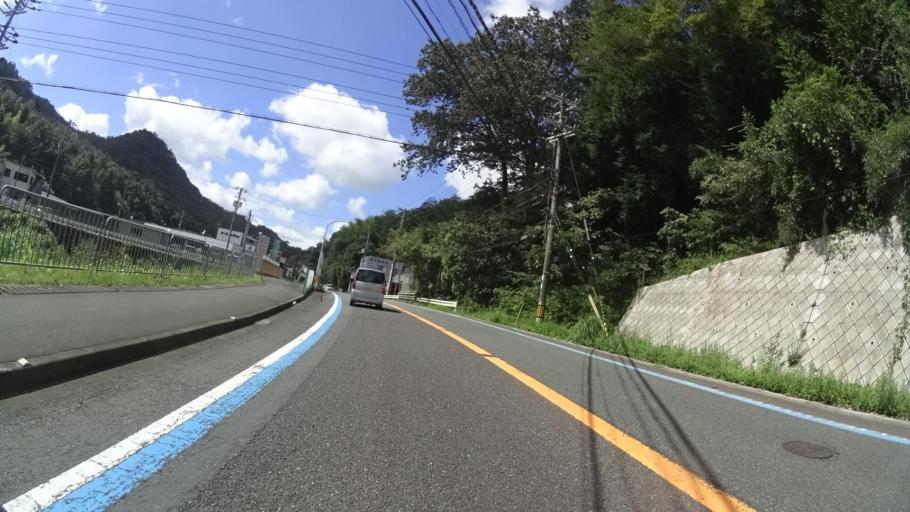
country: JP
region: Kyoto
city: Maizuru
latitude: 35.4483
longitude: 135.2875
